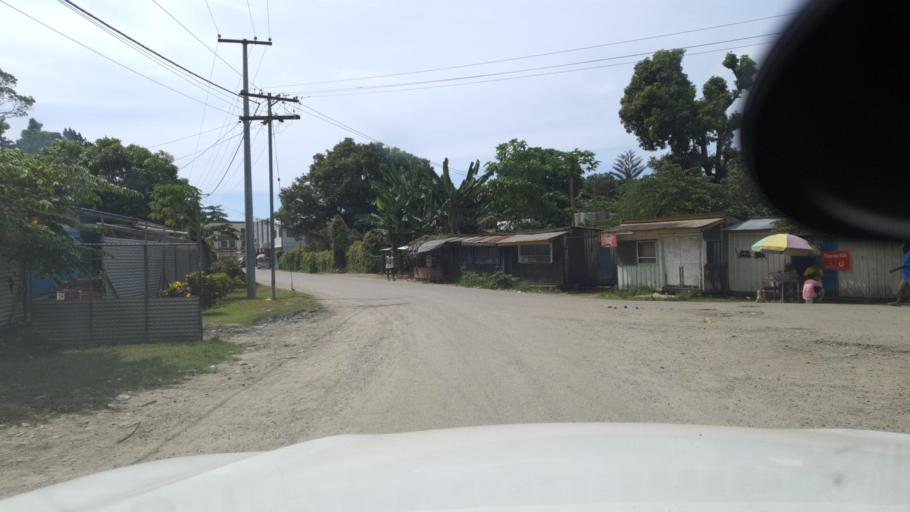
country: SB
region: Guadalcanal
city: Honiara
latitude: -9.4255
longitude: 159.9213
